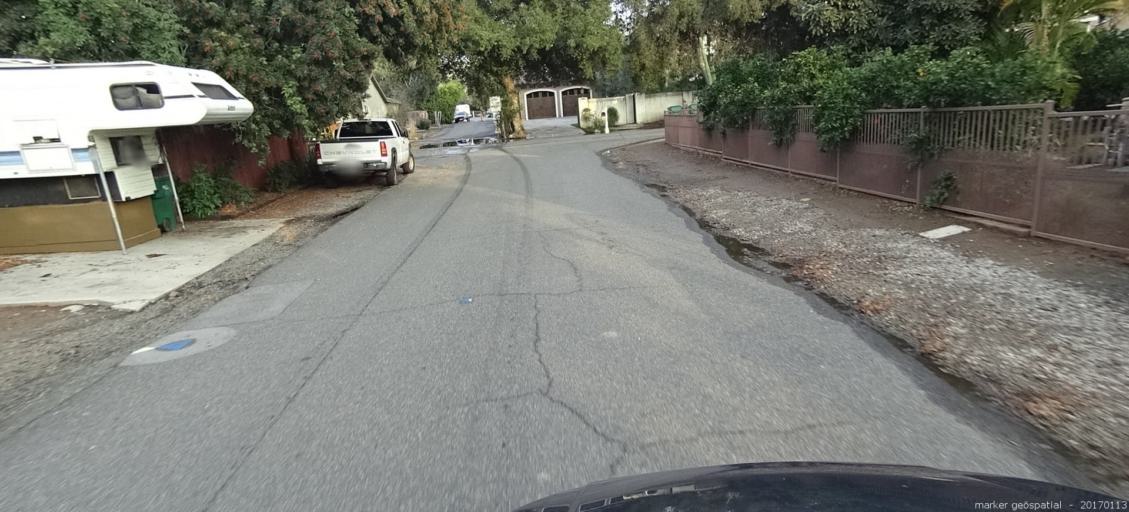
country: US
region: California
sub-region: Orange County
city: Villa Park
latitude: 33.8128
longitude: -117.7812
